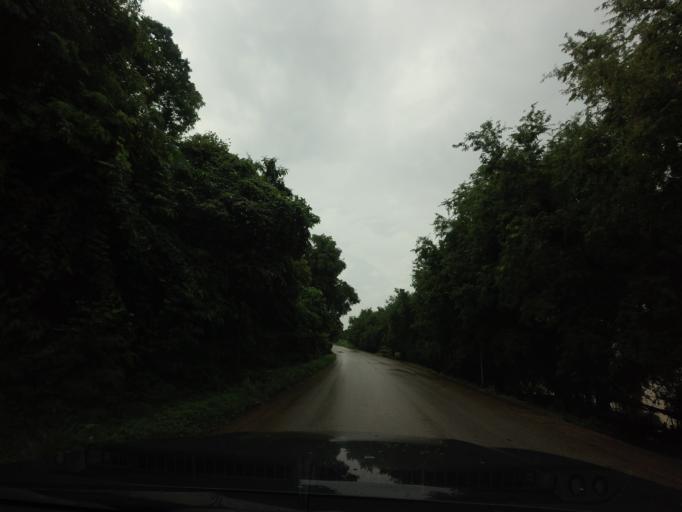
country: TH
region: Loei
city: Pak Chom
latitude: 18.1153
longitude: 101.9903
